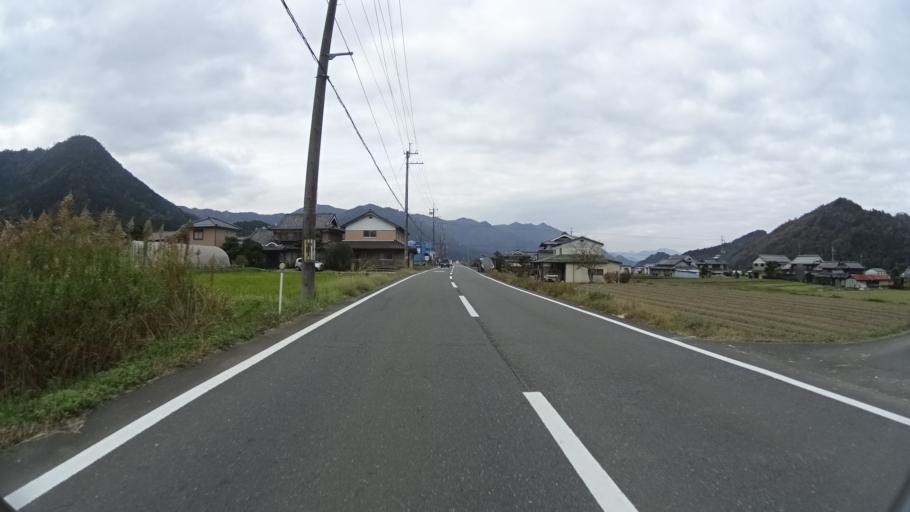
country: JP
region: Hyogo
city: Sasayama
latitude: 35.1434
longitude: 135.1429
